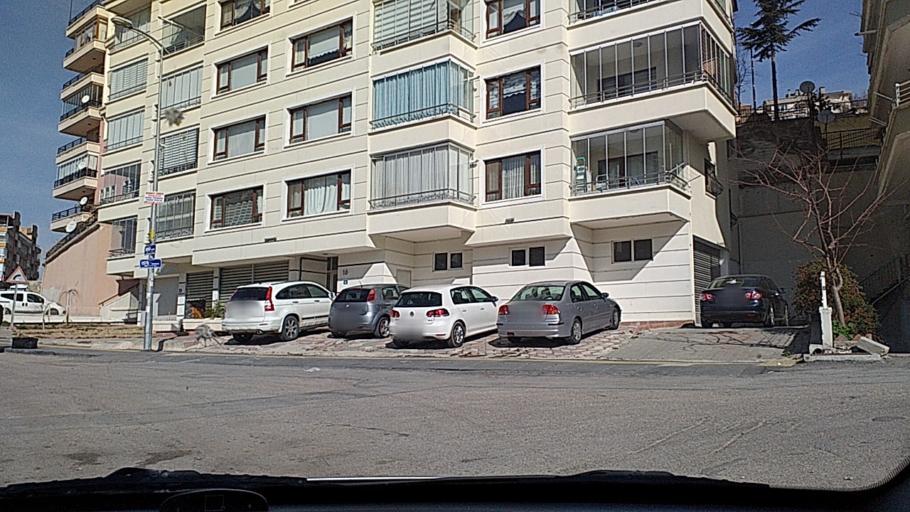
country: TR
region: Ankara
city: Ankara
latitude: 39.9885
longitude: 32.8140
